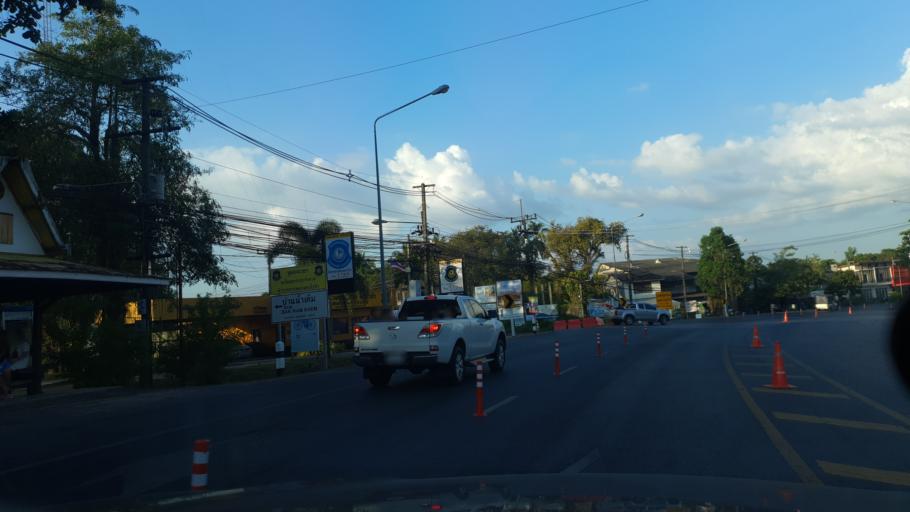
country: TH
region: Phangnga
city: Takua Pa
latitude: 8.8401
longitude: 98.2837
